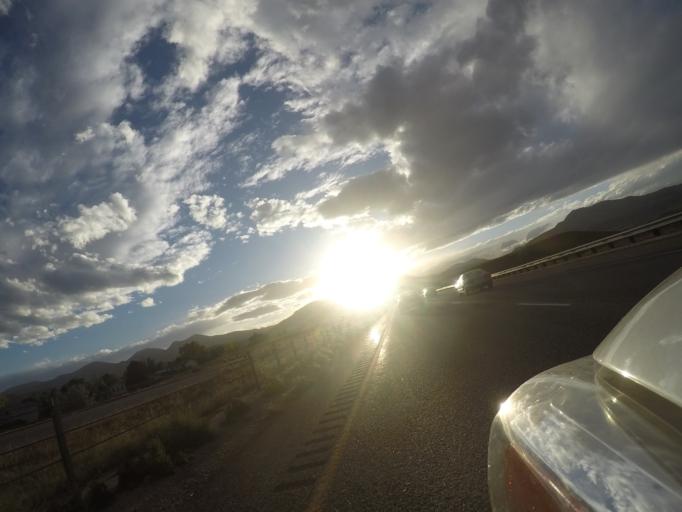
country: US
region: Colorado
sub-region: Jefferson County
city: Ken Caryl
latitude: 39.6392
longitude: -105.1419
